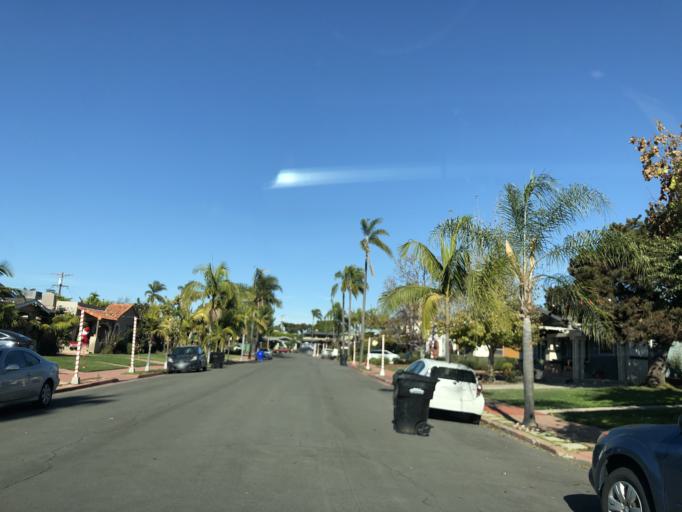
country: US
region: California
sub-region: San Diego County
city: San Diego
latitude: 32.7309
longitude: -117.1278
